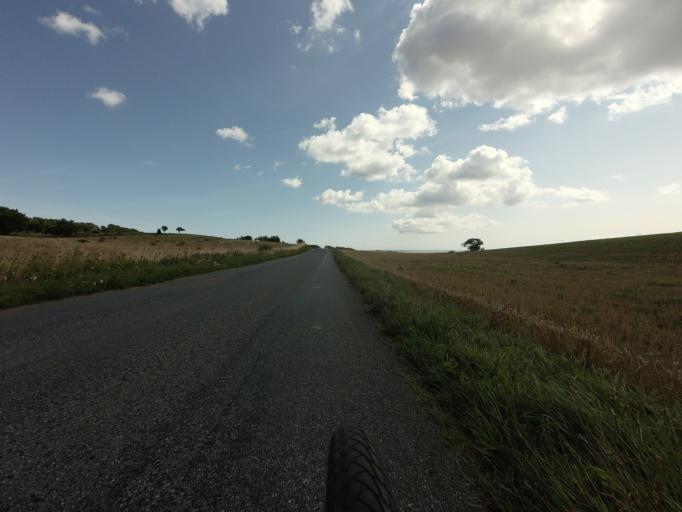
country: DK
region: Zealand
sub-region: Vordingborg Kommune
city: Stege
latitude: 54.9606
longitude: 12.5077
